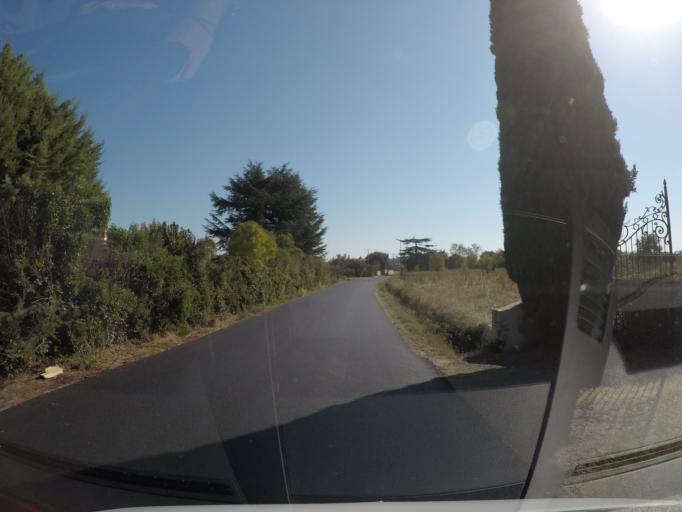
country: FR
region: Languedoc-Roussillon
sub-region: Departement du Gard
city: Ribaute-les-Tavernes
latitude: 44.0243
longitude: 4.0826
